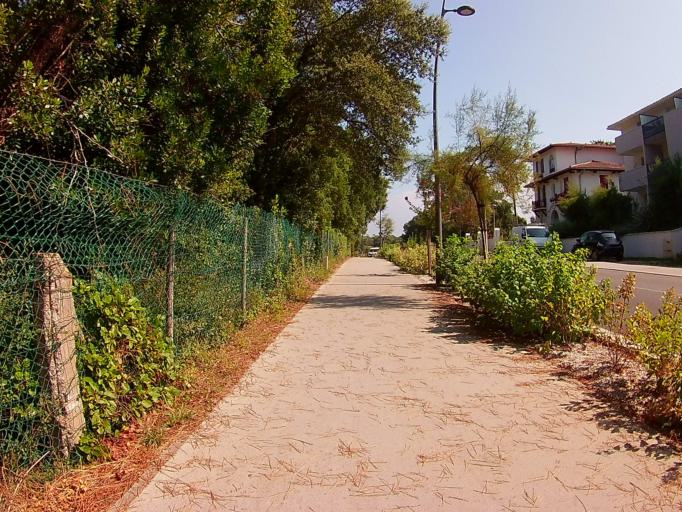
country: FR
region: Aquitaine
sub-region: Departement des Landes
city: Ondres
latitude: 43.5974
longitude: -1.4672
